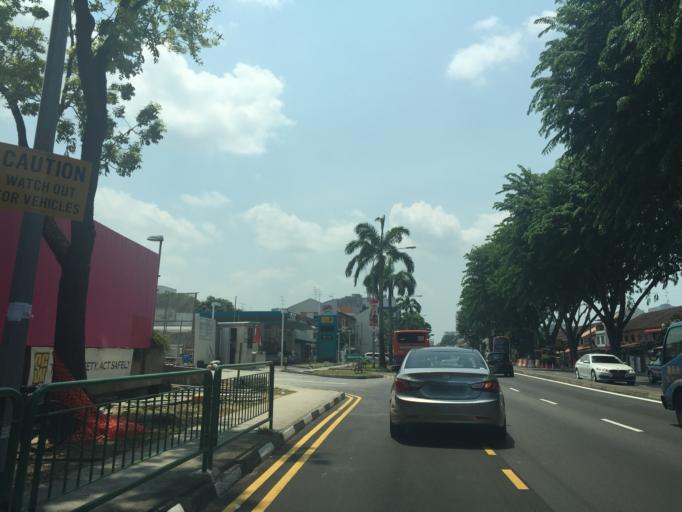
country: SG
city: Singapore
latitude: 1.3316
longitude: 103.8797
